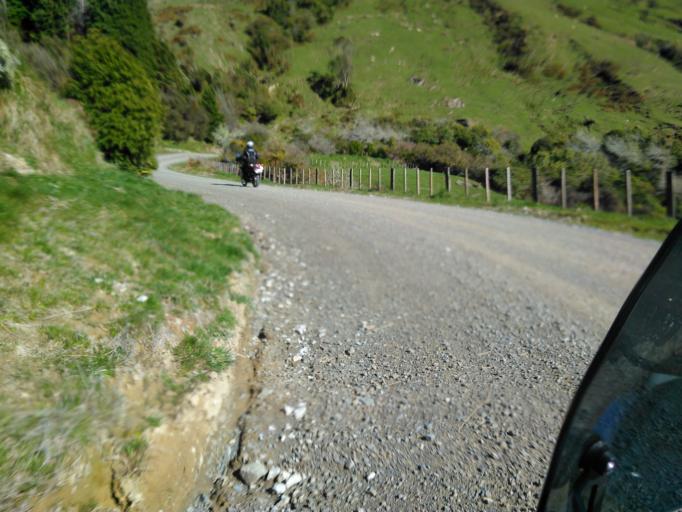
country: NZ
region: Bay of Plenty
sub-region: Opotiki District
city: Opotiki
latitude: -38.3470
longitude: 177.5844
